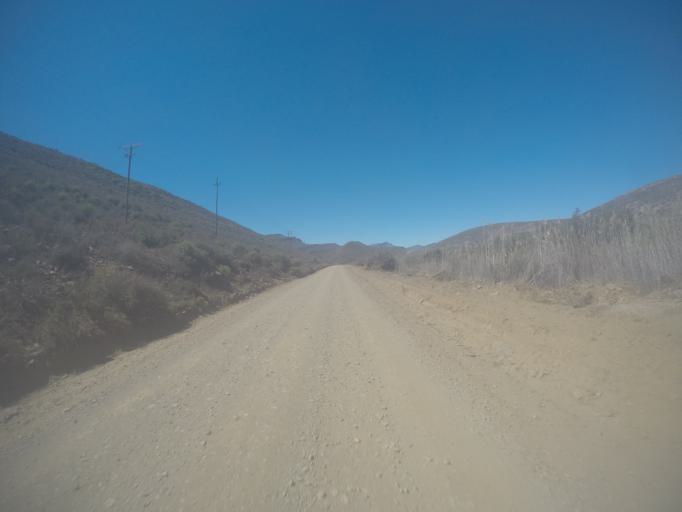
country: ZA
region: Western Cape
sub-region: West Coast District Municipality
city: Clanwilliam
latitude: -32.5152
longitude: 19.3477
